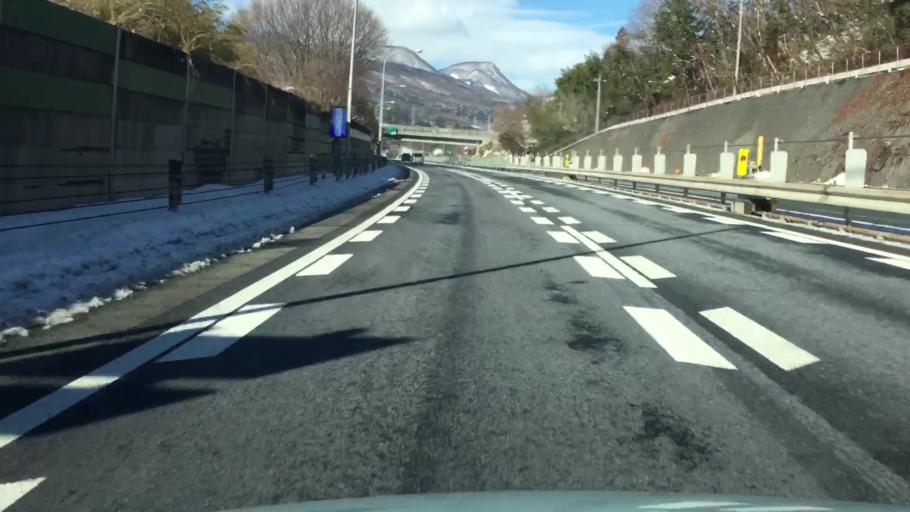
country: JP
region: Gunma
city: Numata
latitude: 36.6986
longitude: 138.9900
